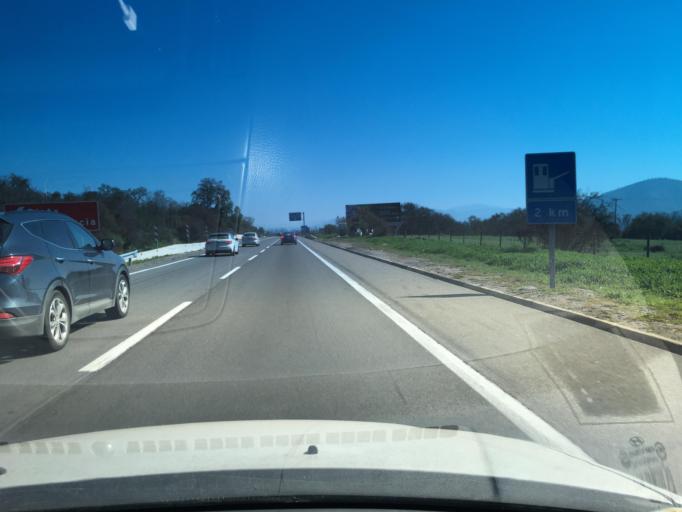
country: CL
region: Santiago Metropolitan
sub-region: Provincia de Melipilla
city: Melipilla
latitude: -33.3781
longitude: -71.2821
